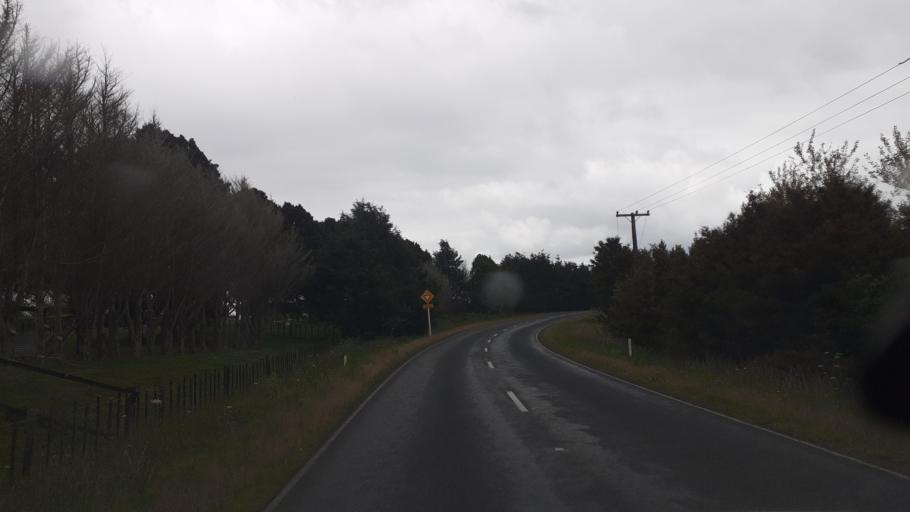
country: NZ
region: Northland
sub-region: Far North District
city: Waimate North
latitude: -35.2779
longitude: 173.8308
